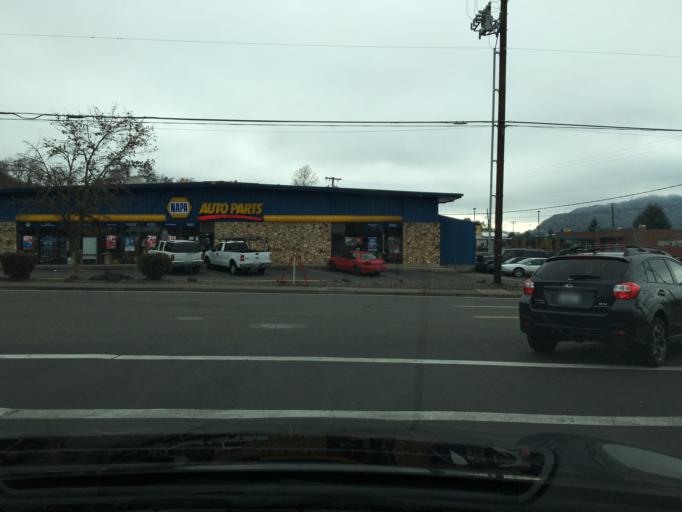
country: US
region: Oregon
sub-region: Douglas County
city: Roseburg
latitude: 43.2270
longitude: -123.3476
